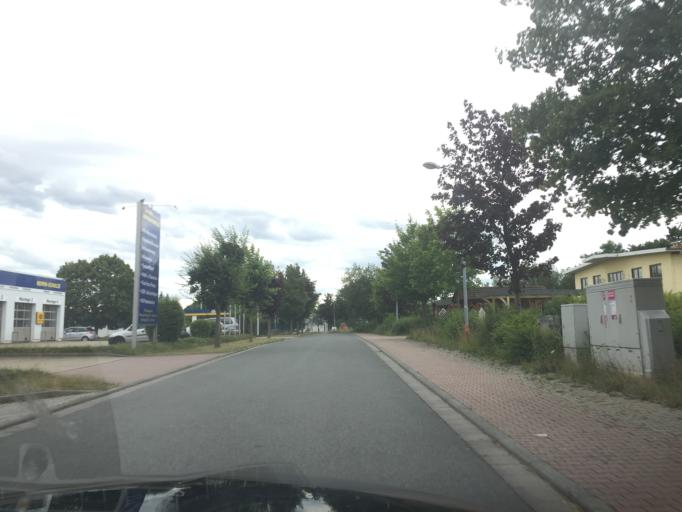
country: DE
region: Thuringia
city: Schmolln
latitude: 50.8838
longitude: 12.3468
